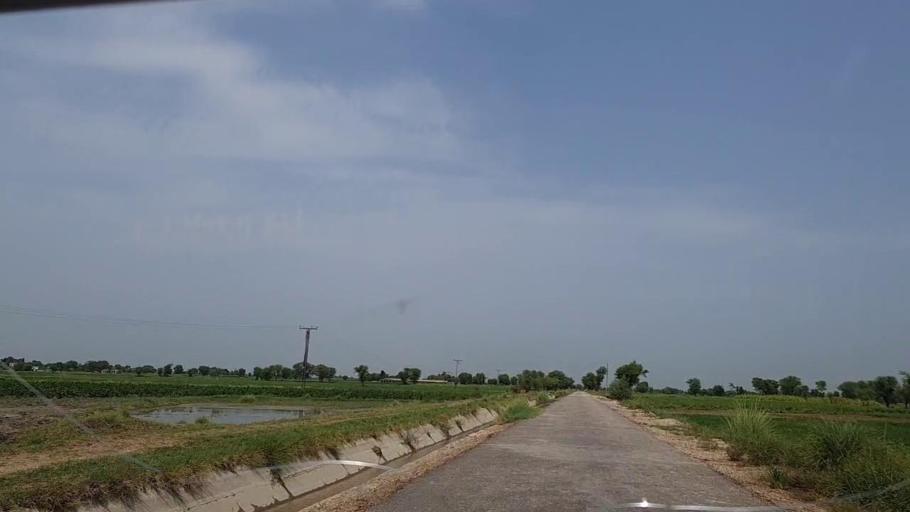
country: PK
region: Sindh
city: Tharu Shah
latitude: 26.9324
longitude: 68.0684
